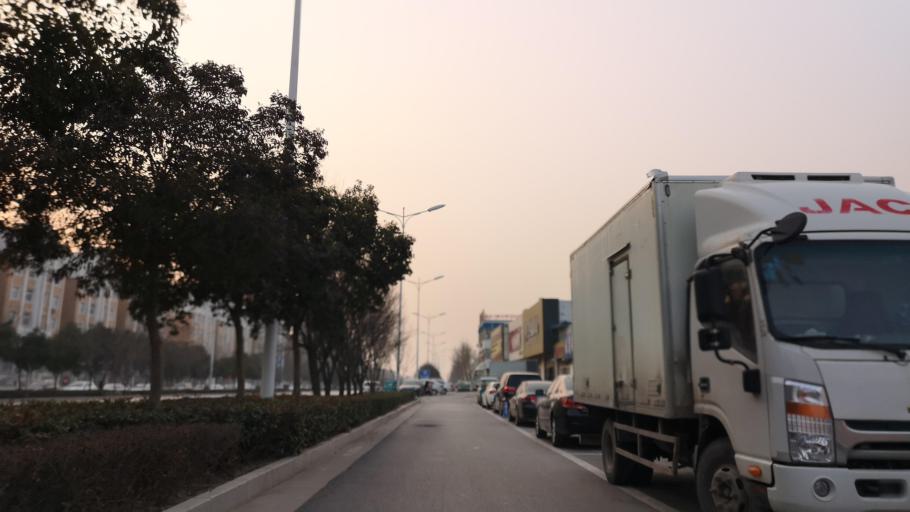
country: CN
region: Henan Sheng
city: Zhongyuanlu
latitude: 35.7892
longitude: 115.0881
